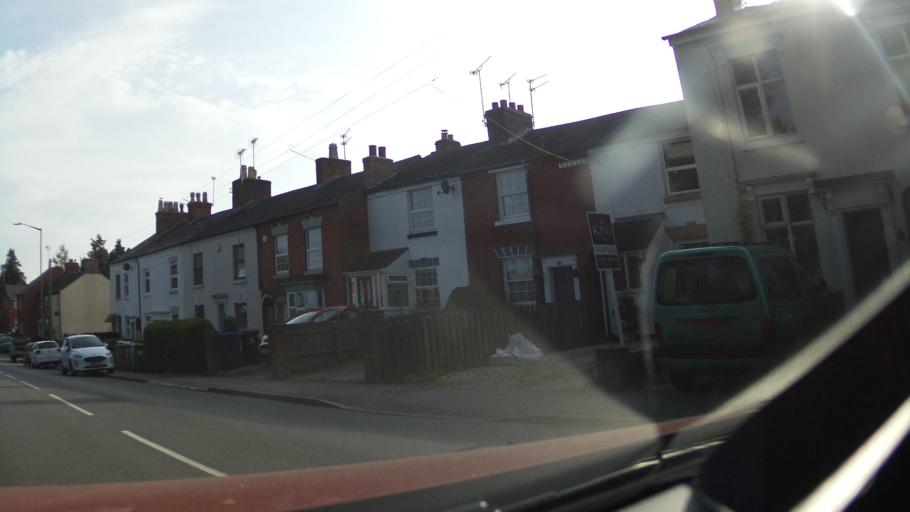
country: GB
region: England
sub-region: Warwickshire
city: Studley
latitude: 52.2690
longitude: -1.8930
